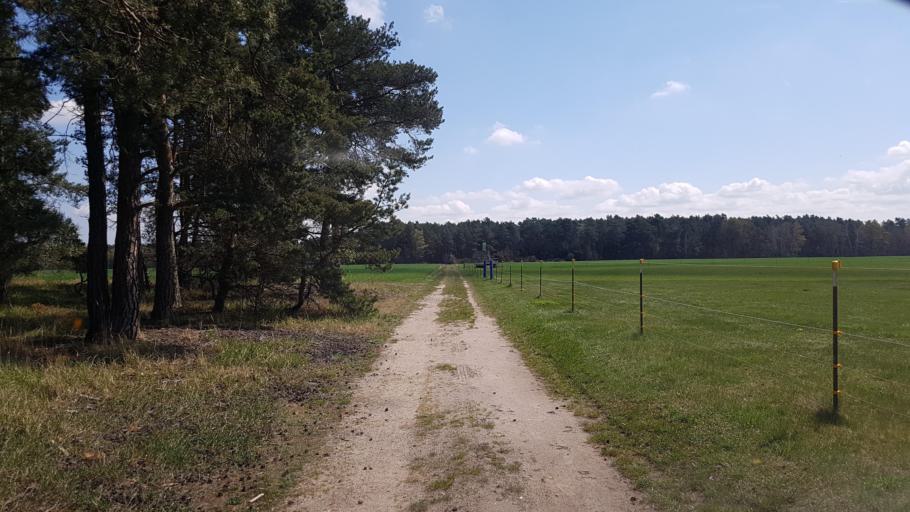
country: DE
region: Brandenburg
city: Bronkow
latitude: 51.6731
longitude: 13.9230
